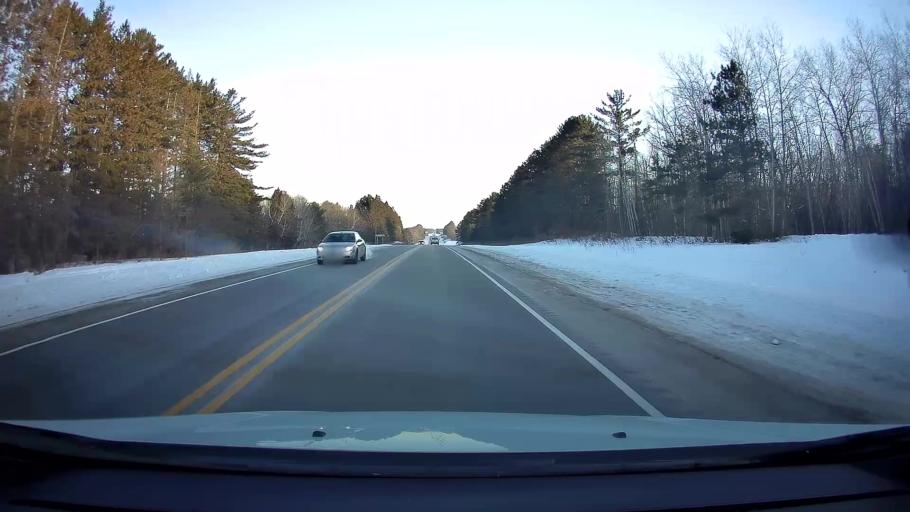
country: US
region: Wisconsin
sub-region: Washburn County
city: Shell Lake
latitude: 45.7536
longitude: -91.9159
